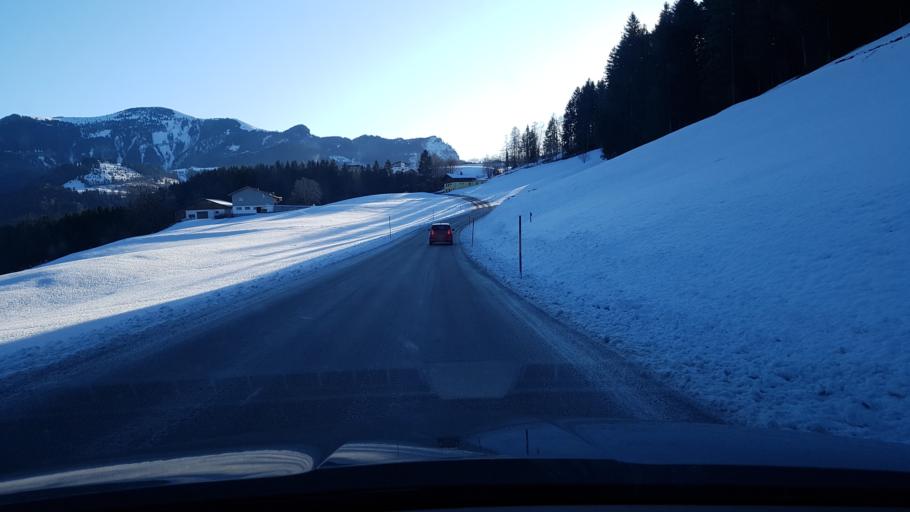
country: AT
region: Salzburg
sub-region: Politischer Bezirk Hallein
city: Kuchl
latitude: 47.6557
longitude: 13.1955
